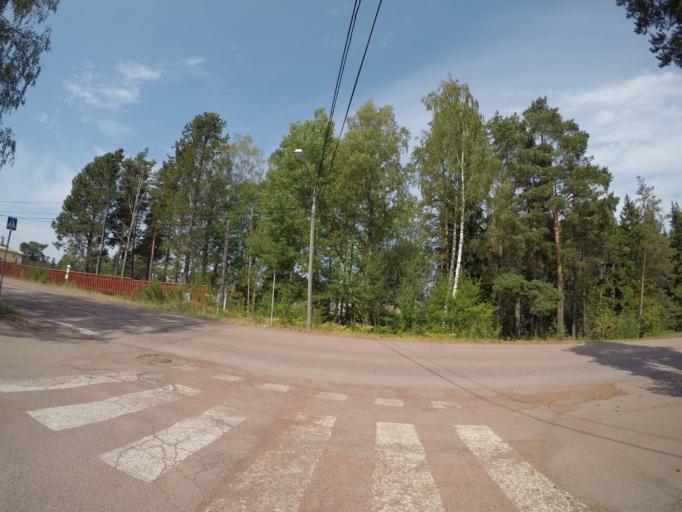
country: AX
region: Alands landsbygd
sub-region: Saltvik
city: Saltvik
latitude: 60.2337
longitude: 20.0010
